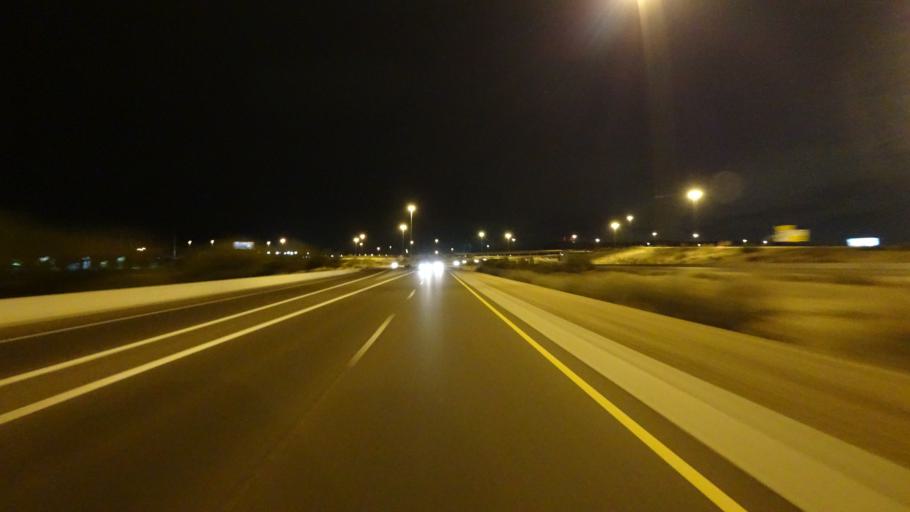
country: US
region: Arizona
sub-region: Maricopa County
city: Guadalupe
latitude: 33.2953
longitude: -111.9652
